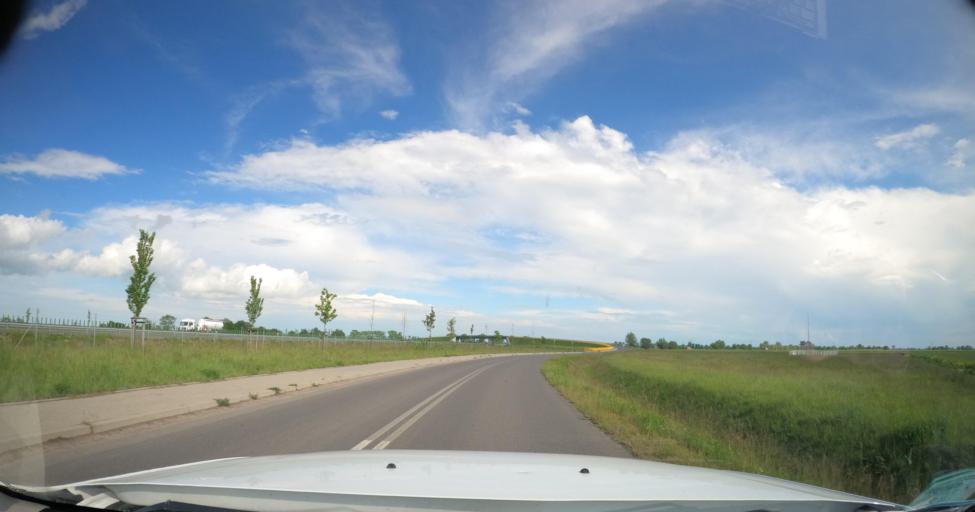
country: PL
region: Pomeranian Voivodeship
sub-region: Powiat nowodworski
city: Nowy Dwor Gdanski
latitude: 54.1888
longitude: 19.1631
